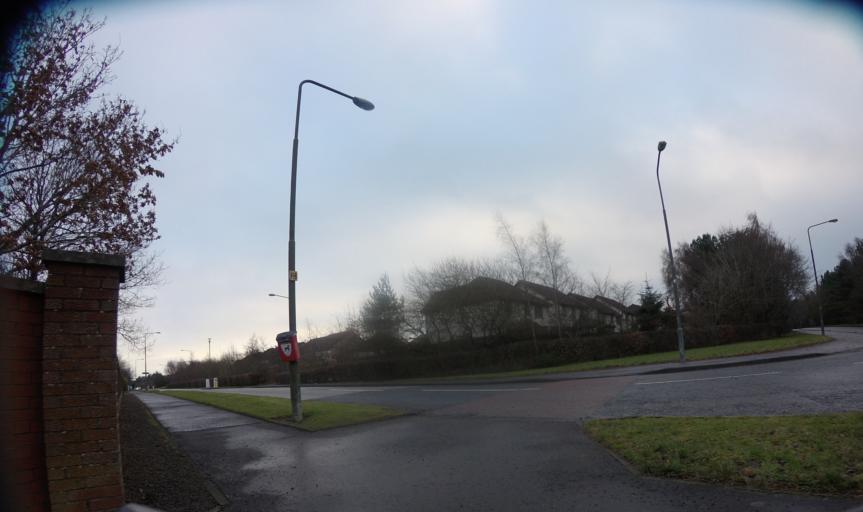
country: GB
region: Scotland
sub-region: West Lothian
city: Livingston
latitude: 55.8736
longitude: -3.5333
